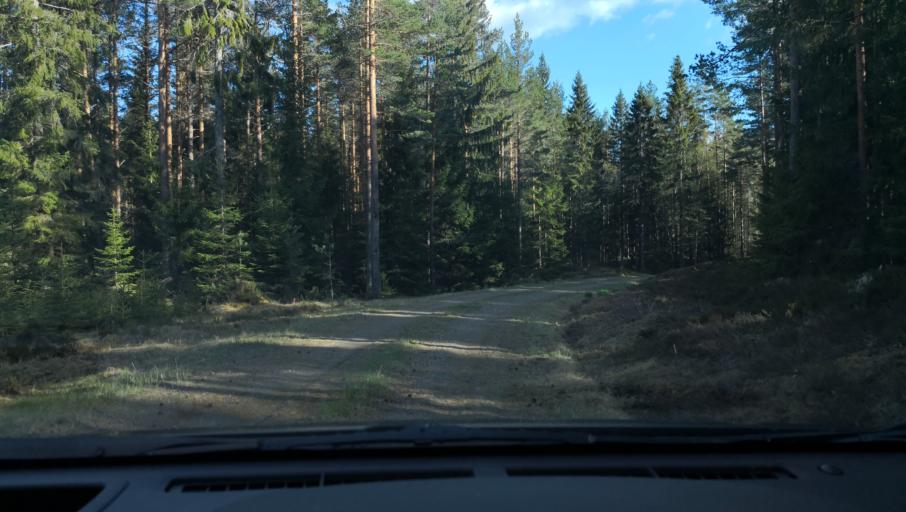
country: SE
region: OErebro
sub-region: Askersunds Kommun
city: Asbro
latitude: 58.8742
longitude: 15.1249
